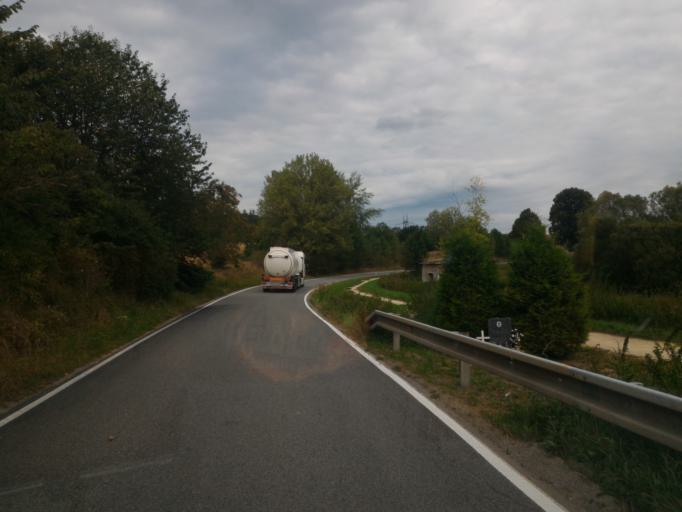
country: CZ
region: Vysocina
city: Zeletava
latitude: 49.1463
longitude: 15.5695
